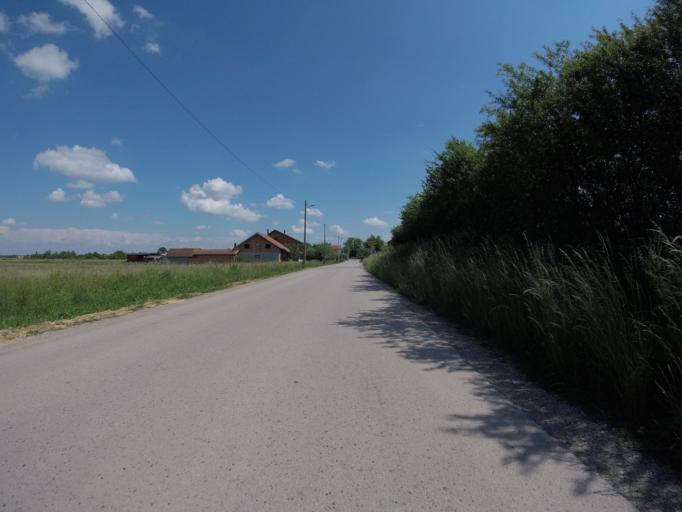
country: HR
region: Zagrebacka
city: Mraclin
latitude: 45.6667
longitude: 16.0819
